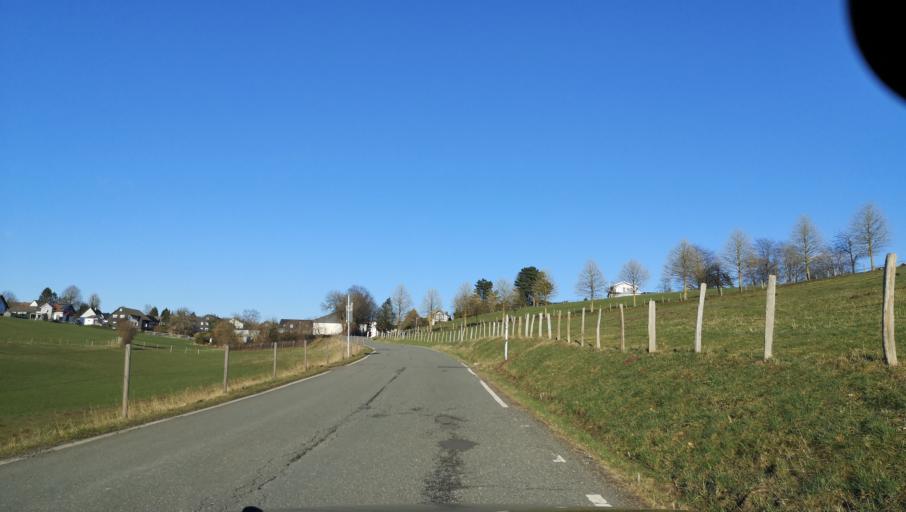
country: DE
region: North Rhine-Westphalia
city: Ennepetal
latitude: 51.2634
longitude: 7.3762
